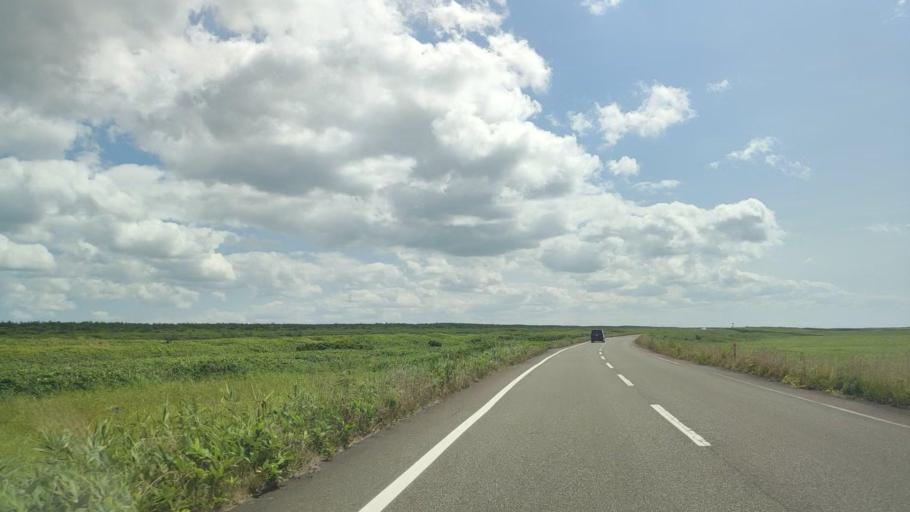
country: JP
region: Hokkaido
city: Wakkanai
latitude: 45.1538
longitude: 141.5919
